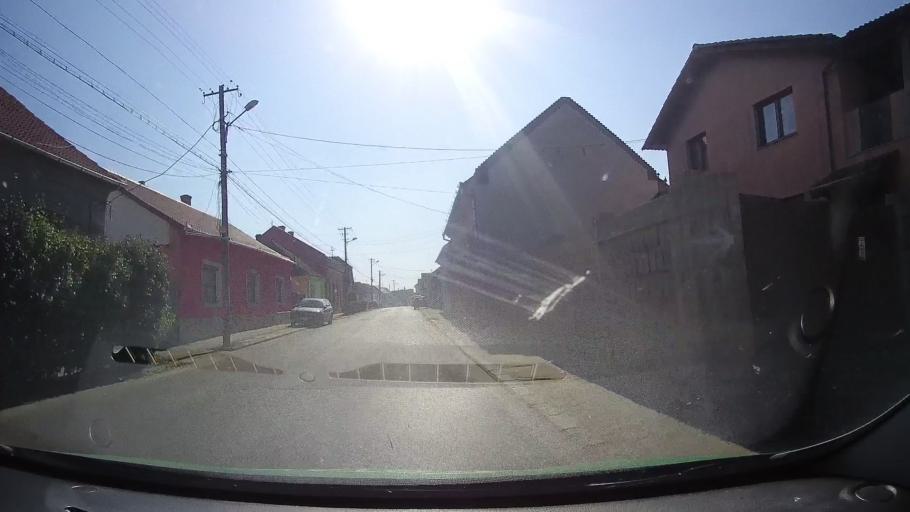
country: RO
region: Arad
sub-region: Oras Lipova
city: Lipova
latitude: 46.0888
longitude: 21.6909
